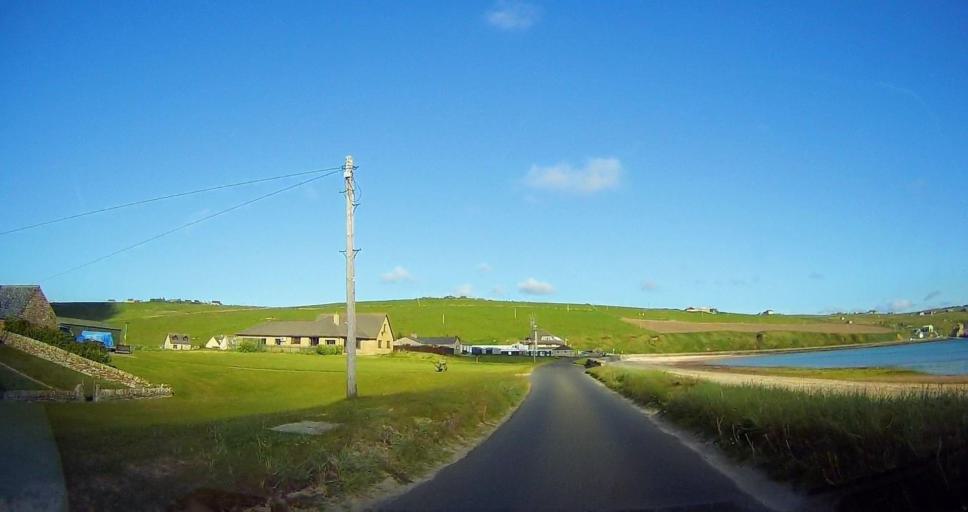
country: GB
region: Scotland
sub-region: Orkney Islands
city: Orkney
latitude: 58.9624
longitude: -2.9750
